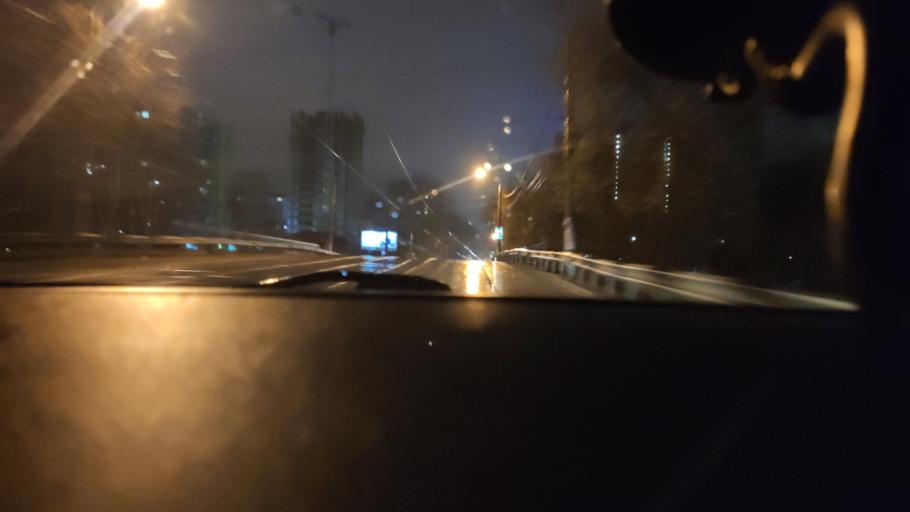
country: RU
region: Perm
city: Perm
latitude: 57.9929
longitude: 56.2182
